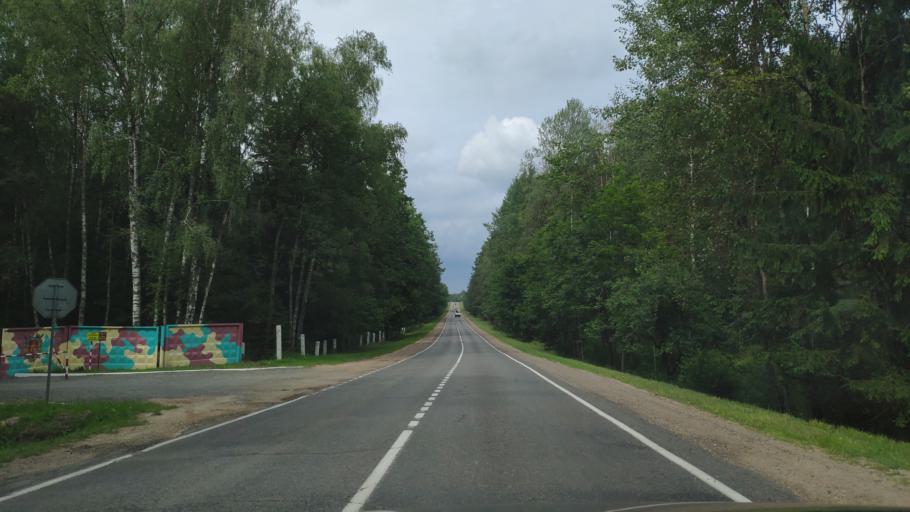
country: BY
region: Minsk
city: Novosel'ye
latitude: 53.9521
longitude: 27.2459
